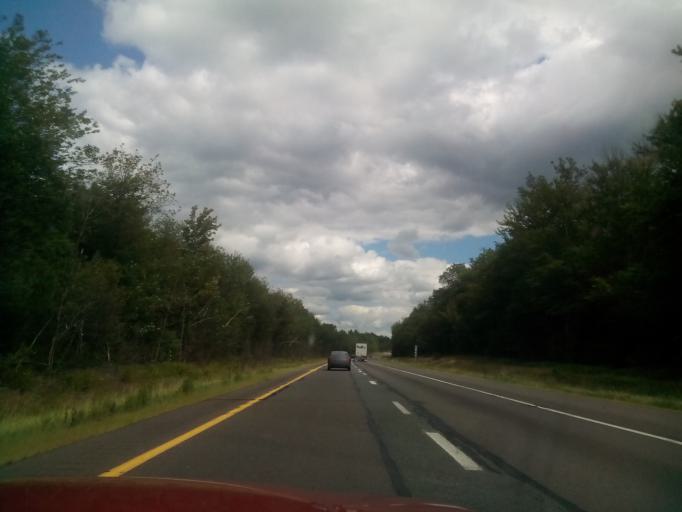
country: US
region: Pennsylvania
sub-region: Carbon County
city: Indian Mountain Lake
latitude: 41.0777
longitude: -75.5295
